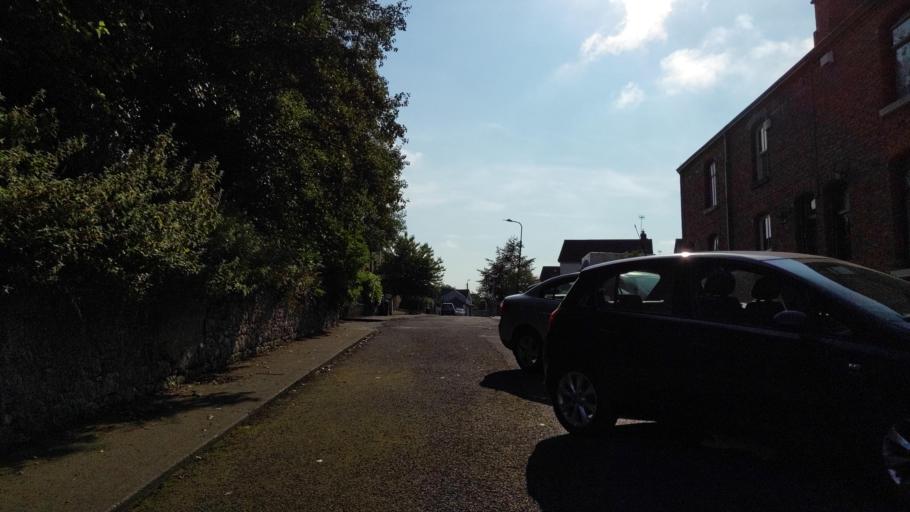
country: IE
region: Leinster
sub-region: Lu
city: Drogheda
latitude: 53.7093
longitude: -6.3468
